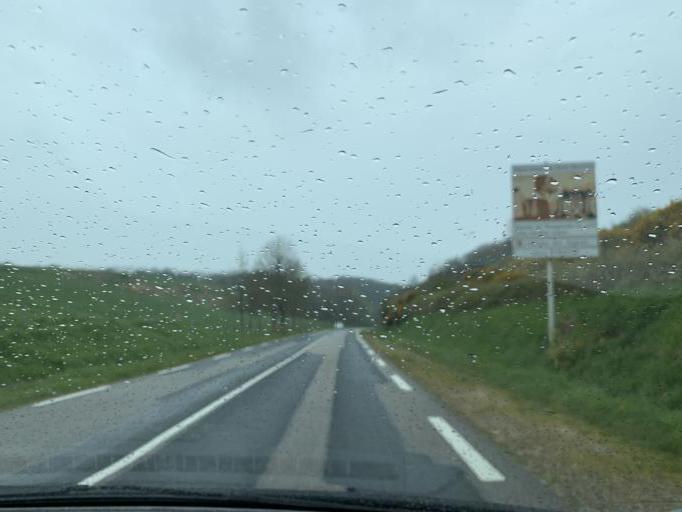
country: FR
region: Haute-Normandie
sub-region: Departement de la Seine-Maritime
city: Etretat
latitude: 49.6976
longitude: 0.2030
